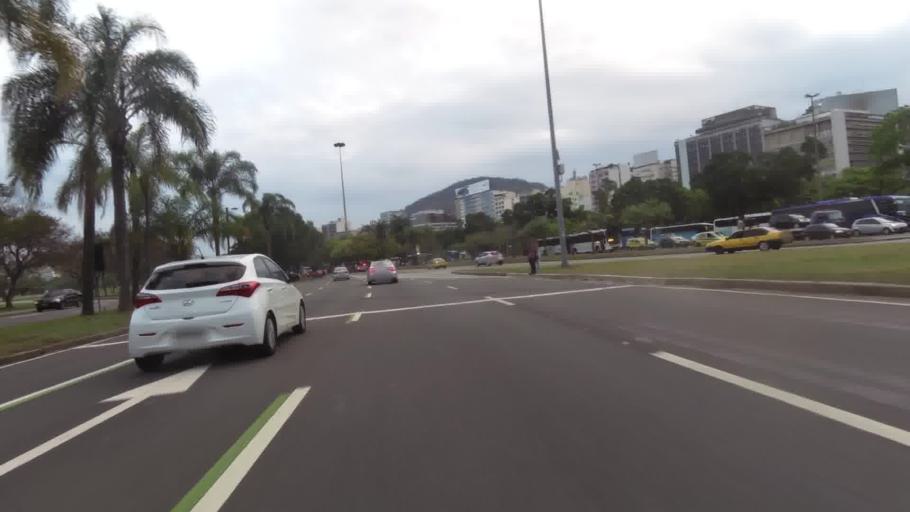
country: BR
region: Rio de Janeiro
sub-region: Rio De Janeiro
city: Rio de Janeiro
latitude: -22.9140
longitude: -43.1741
